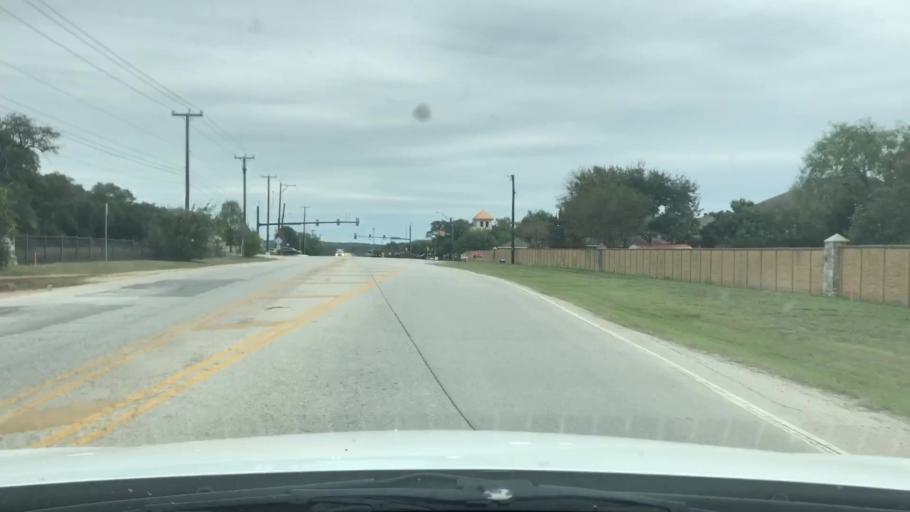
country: US
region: Texas
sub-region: Bexar County
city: Hollywood Park
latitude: 29.6457
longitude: -98.4042
